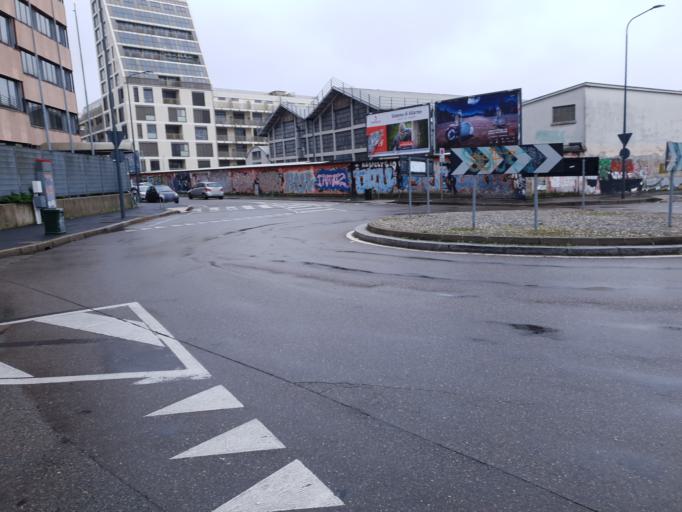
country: IT
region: Lombardy
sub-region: Citta metropolitana di Milano
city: Cormano
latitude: 45.5081
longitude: 9.1677
